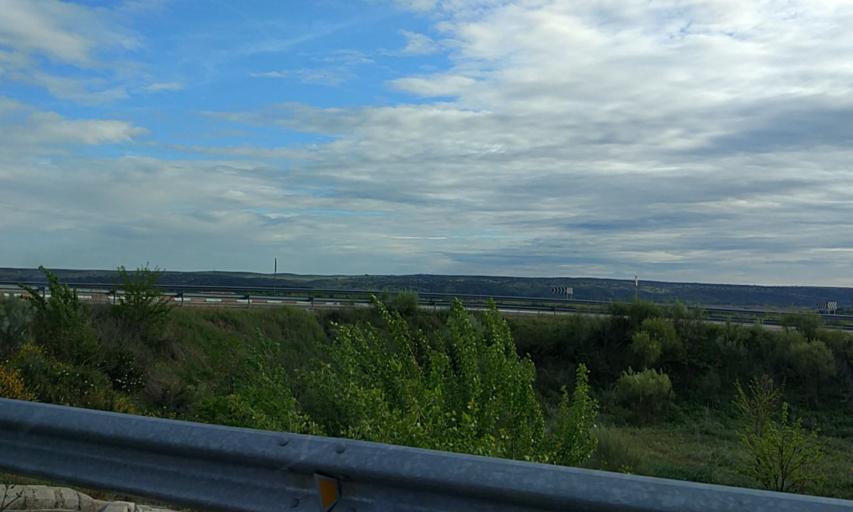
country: ES
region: Extremadura
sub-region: Provincia de Caceres
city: Coria
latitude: 40.0092
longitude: -6.5616
